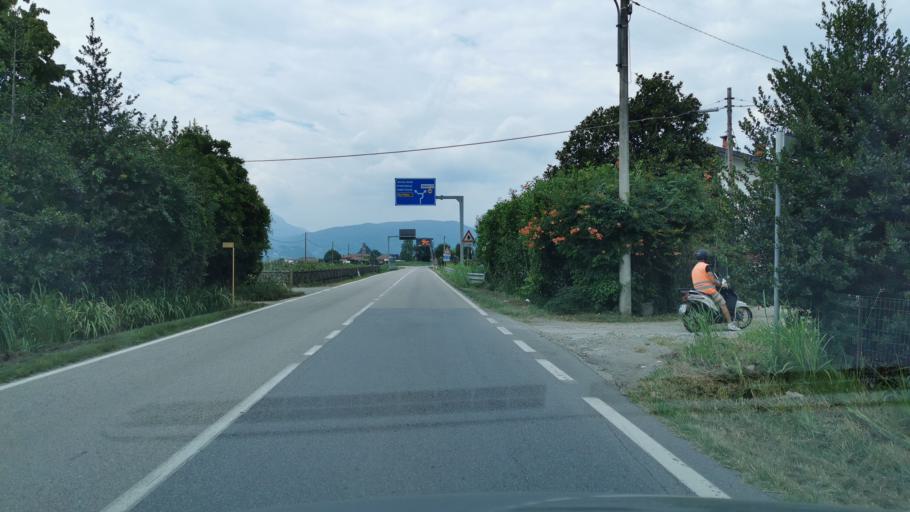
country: IT
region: Piedmont
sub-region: Provincia di Torino
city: Osasco
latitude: 44.8411
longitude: 7.3539
